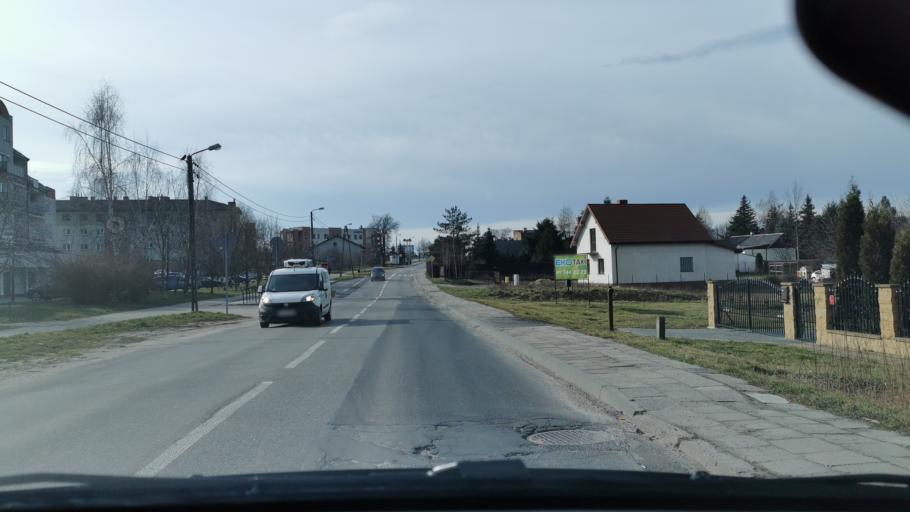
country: PL
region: Lublin Voivodeship
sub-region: Powiat lubelski
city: Lublin
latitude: 51.2017
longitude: 22.5428
